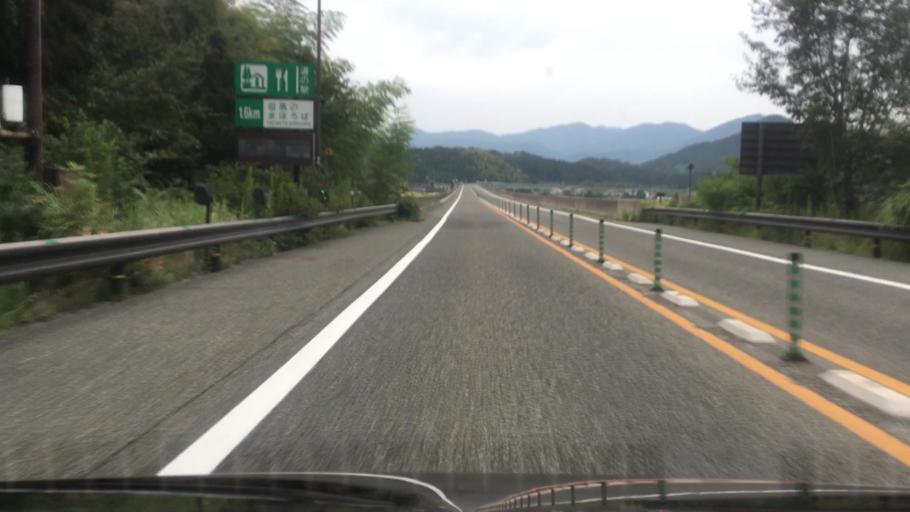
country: JP
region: Kyoto
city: Fukuchiyama
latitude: 35.3054
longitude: 134.8897
